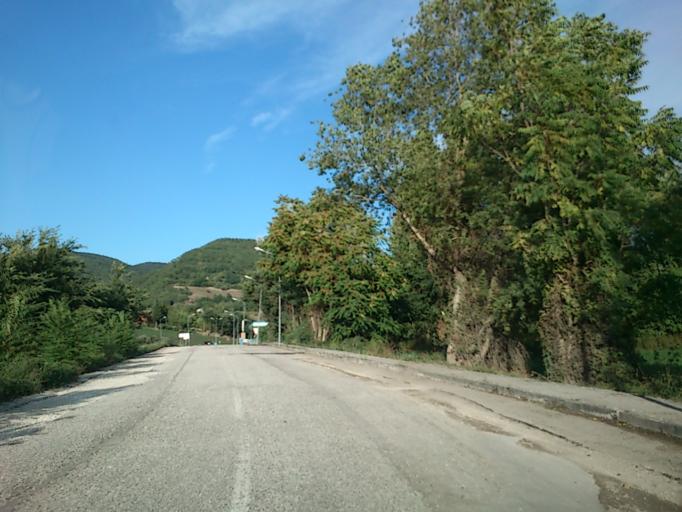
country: IT
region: The Marches
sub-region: Provincia di Pesaro e Urbino
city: Canavaccio
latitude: 43.6901
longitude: 12.7062
